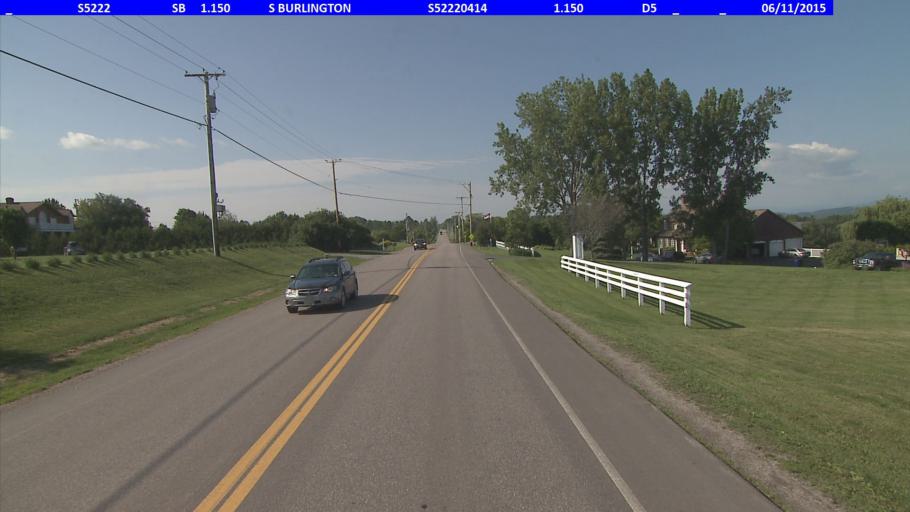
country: US
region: Vermont
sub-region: Chittenden County
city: South Burlington
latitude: 44.4331
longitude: -73.1924
